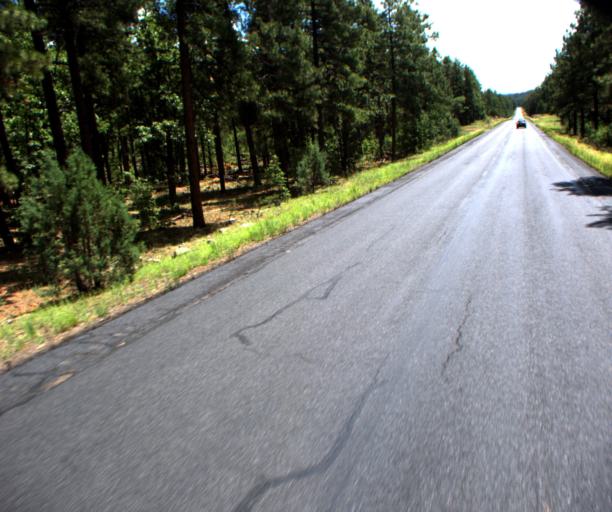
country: US
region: Arizona
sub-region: Gila County
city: Pine
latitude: 34.4832
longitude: -111.4541
